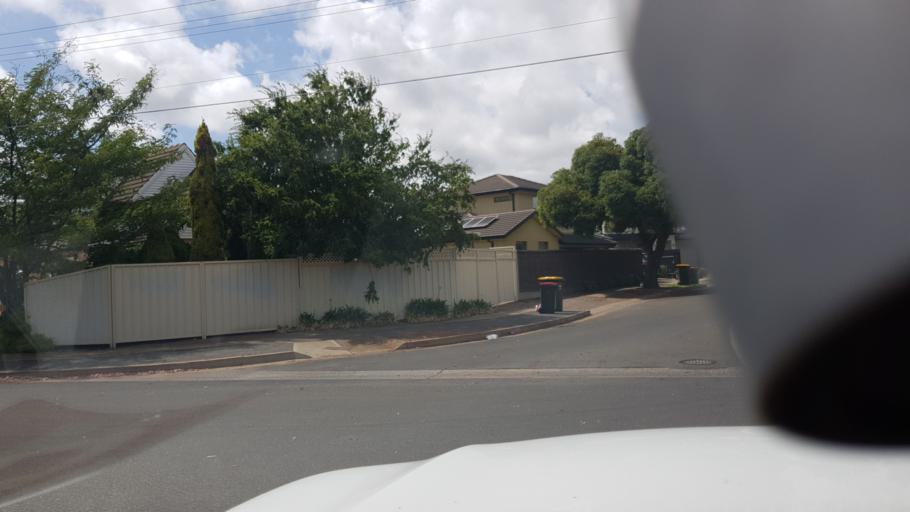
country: AU
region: South Australia
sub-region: Adelaide
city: Brighton
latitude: -35.0199
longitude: 138.5312
